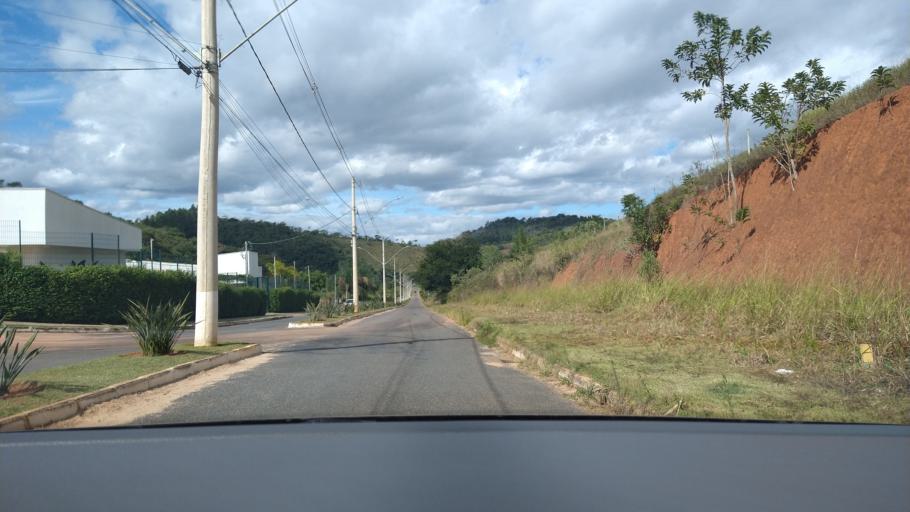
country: BR
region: Minas Gerais
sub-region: Vicosa
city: Vicosa
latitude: -20.7817
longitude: -42.8482
